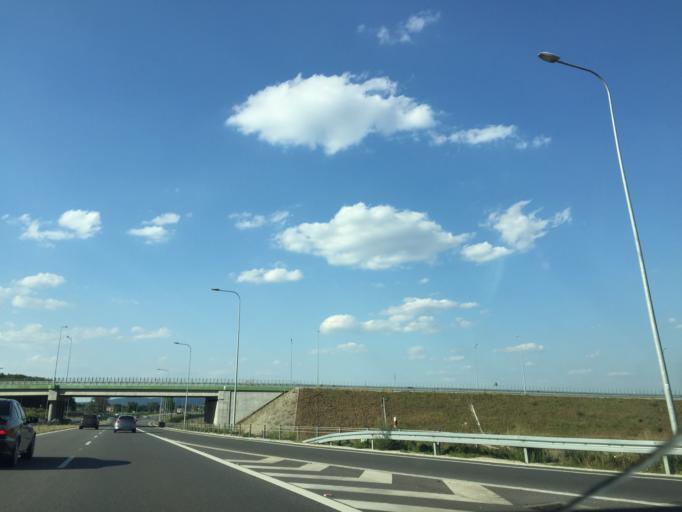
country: PL
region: Swietokrzyskie
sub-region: Powiat jedrzejowski
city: Sobkow
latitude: 50.7295
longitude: 20.4086
